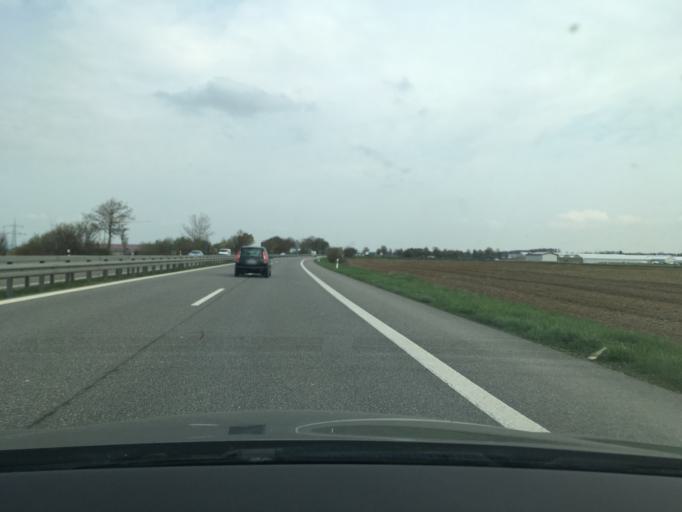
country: DE
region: Baden-Wuerttemberg
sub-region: Tuebingen Region
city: Mietingen
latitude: 48.1940
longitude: 9.8719
